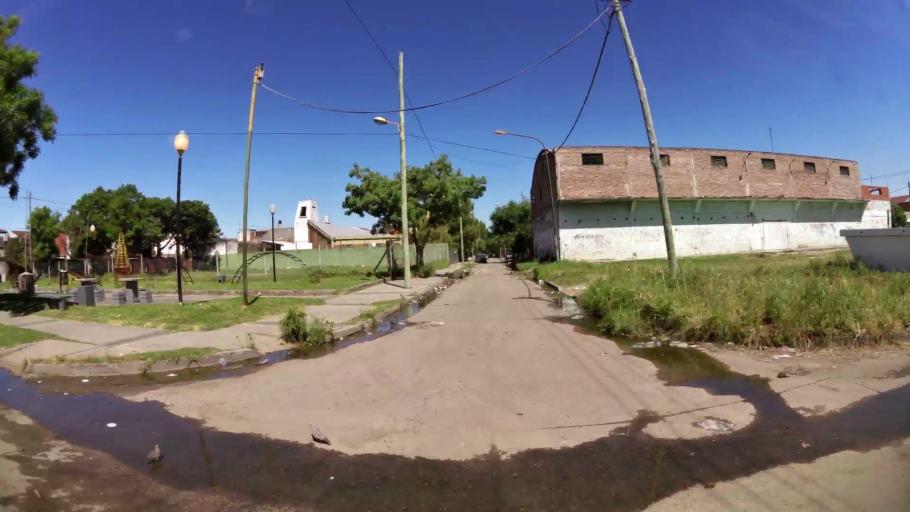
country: AR
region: Buenos Aires
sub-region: Partido de General San Martin
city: General San Martin
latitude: -34.5276
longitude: -58.5661
